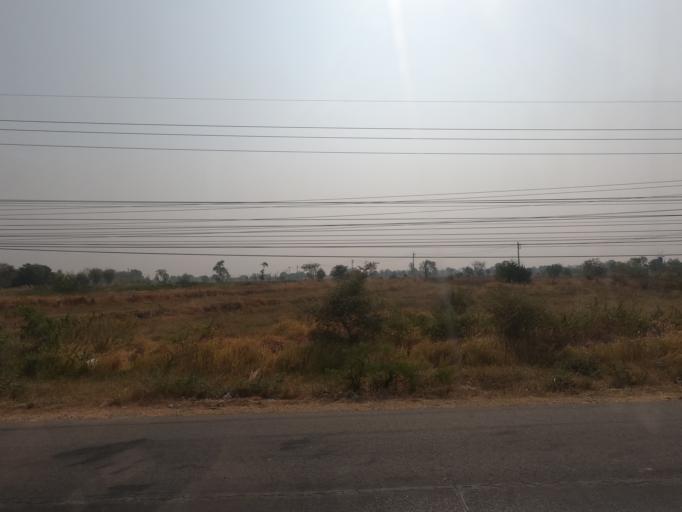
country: TH
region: Khon Kaen
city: Phon
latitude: 15.8886
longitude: 102.6441
